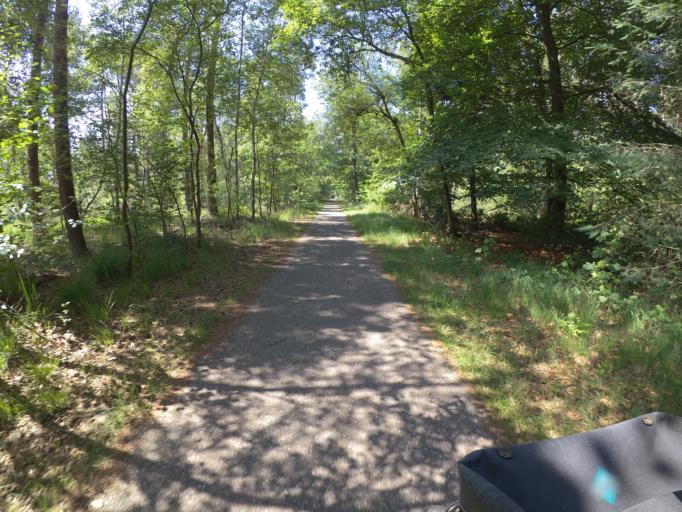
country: NL
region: North Brabant
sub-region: Gemeente Haaren
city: Haaren
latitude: 51.5683
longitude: 5.2313
